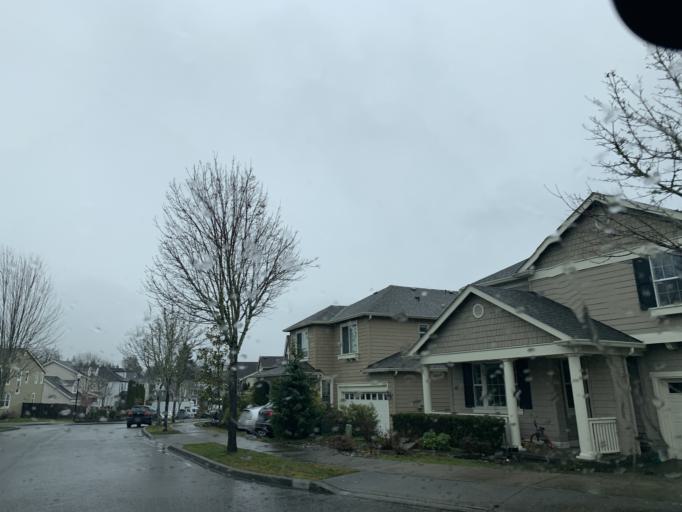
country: US
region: Washington
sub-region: King County
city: Woodinville
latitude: 47.7393
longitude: -122.1675
